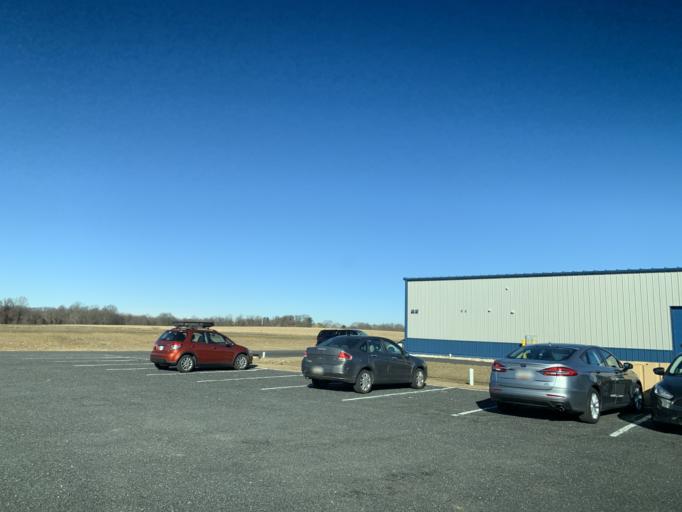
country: US
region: Maryland
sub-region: Harford County
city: Aberdeen
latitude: 39.5688
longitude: -76.2057
